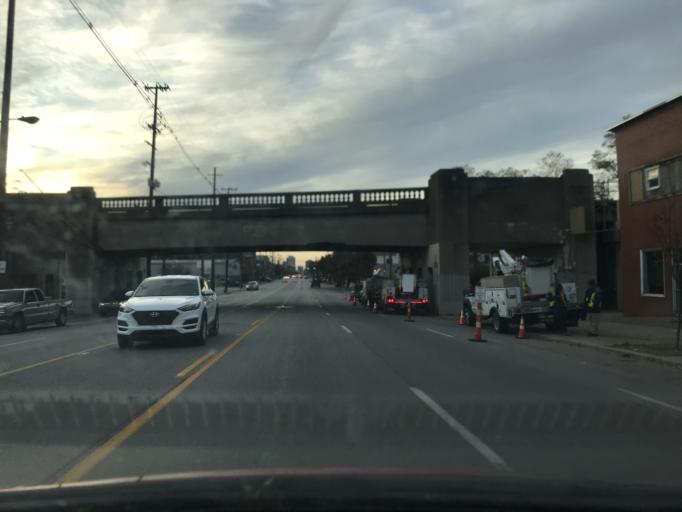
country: US
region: Kentucky
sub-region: Jefferson County
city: Louisville
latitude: 38.2444
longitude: -85.7348
